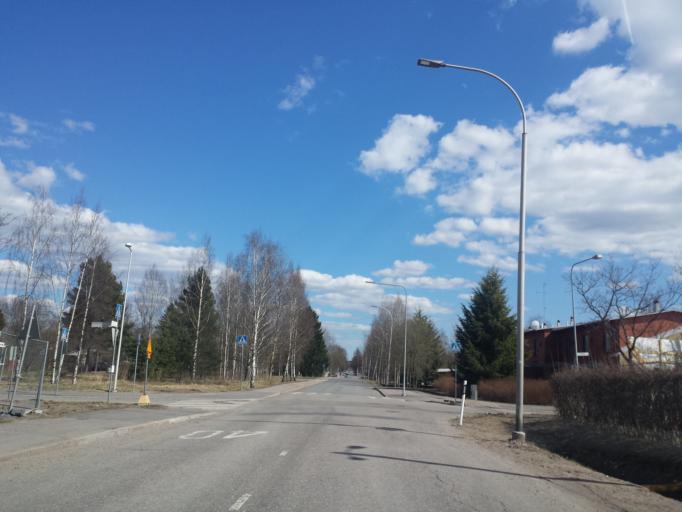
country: FI
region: Uusimaa
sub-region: Helsinki
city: Vantaa
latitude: 60.2941
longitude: 25.0109
